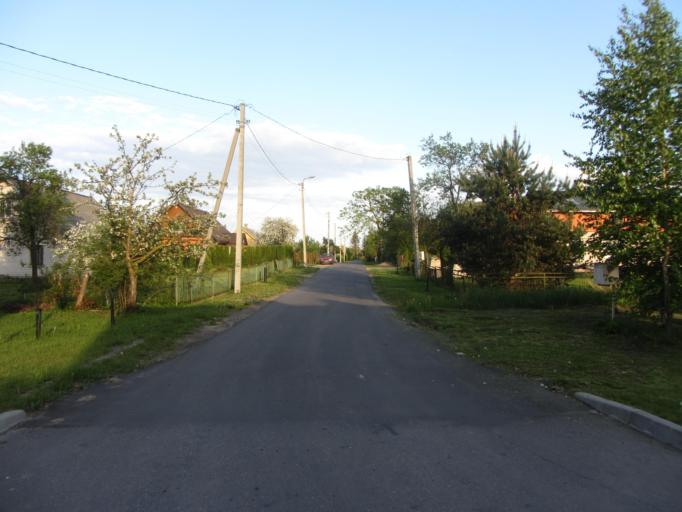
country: LT
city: Sirvintos
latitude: 55.0345
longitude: 24.9749
